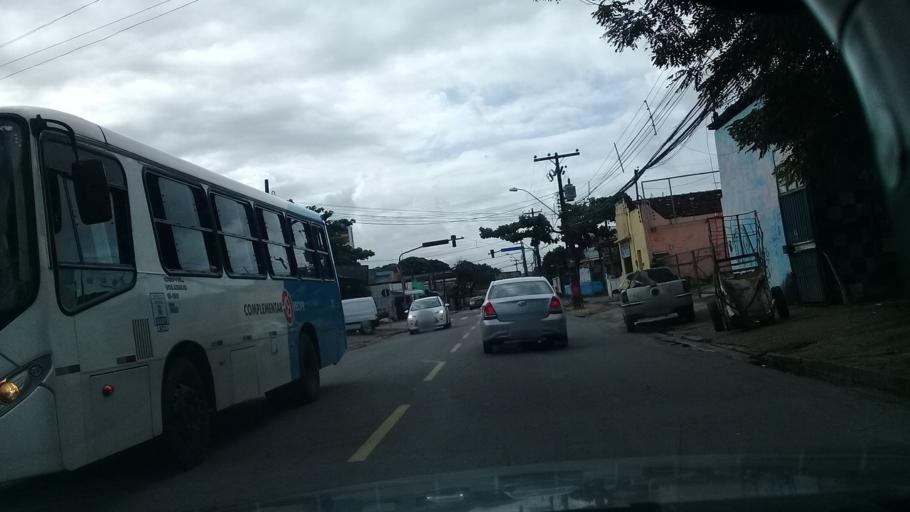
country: BR
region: Pernambuco
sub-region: Recife
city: Recife
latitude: -8.0360
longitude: -34.8802
